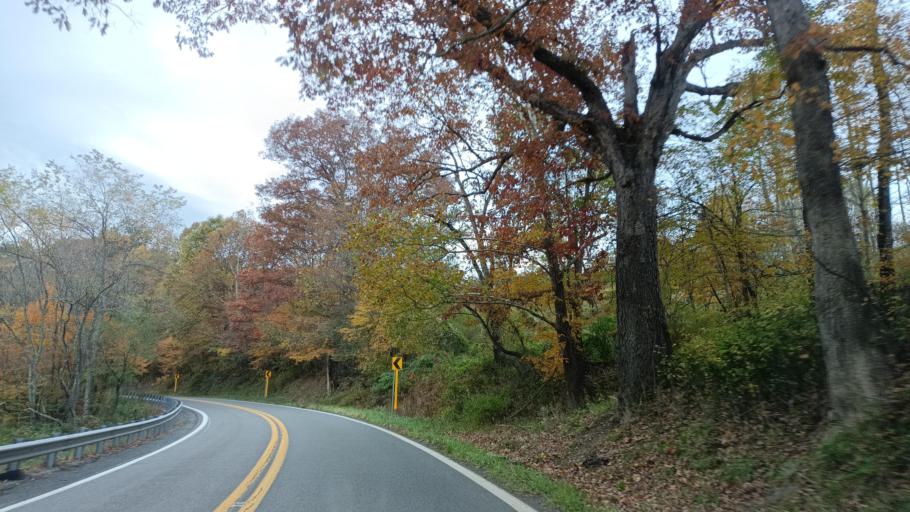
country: US
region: West Virginia
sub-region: Taylor County
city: Grafton
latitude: 39.3345
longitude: -79.8919
